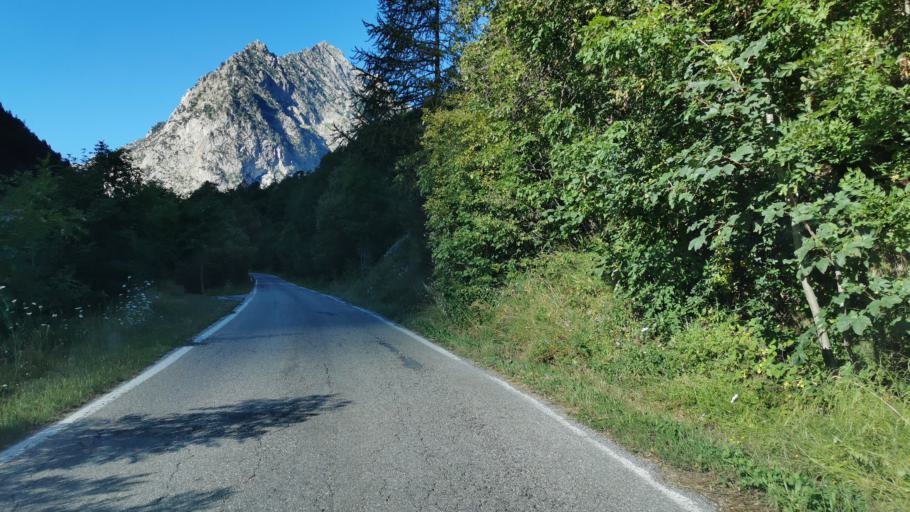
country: IT
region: Piedmont
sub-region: Provincia di Cuneo
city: Demonte
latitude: 44.2162
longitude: 7.2801
